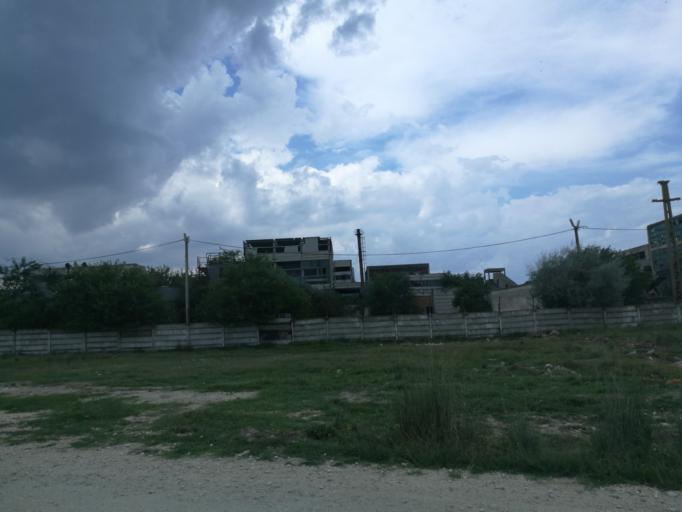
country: RO
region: Constanta
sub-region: Comuna Sacele
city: Sacele
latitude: 44.4464
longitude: 28.7418
